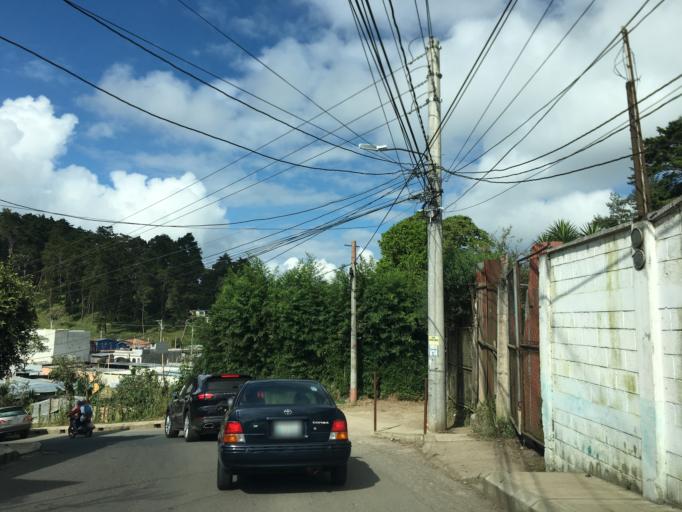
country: GT
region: Guatemala
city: San Jose Pinula
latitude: 14.5606
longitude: -90.4375
